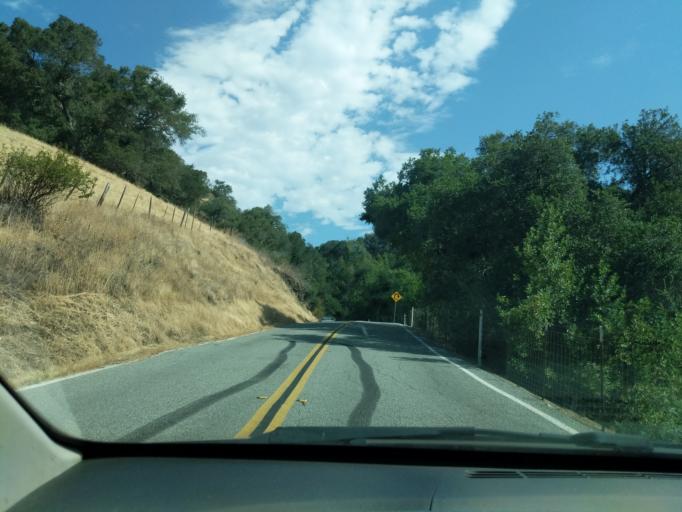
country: US
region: California
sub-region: Santa Clara County
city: Gilroy
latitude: 37.0587
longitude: -121.5207
